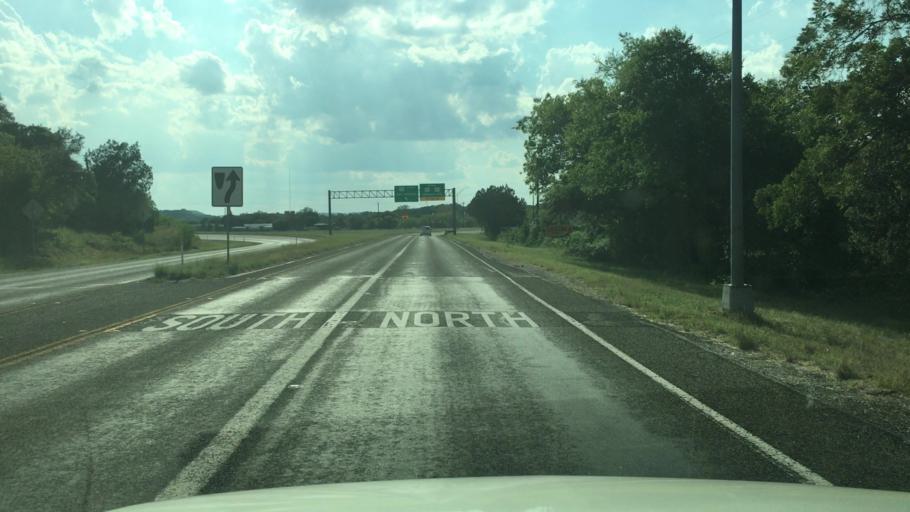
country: US
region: Texas
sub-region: Blanco County
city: Johnson City
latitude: 30.2013
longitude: -98.3727
